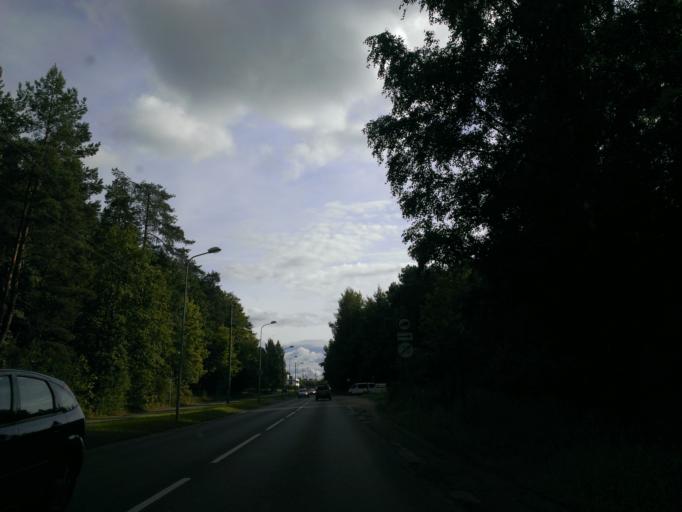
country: LV
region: Stopini
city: Ulbroka
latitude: 56.9626
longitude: 24.2527
